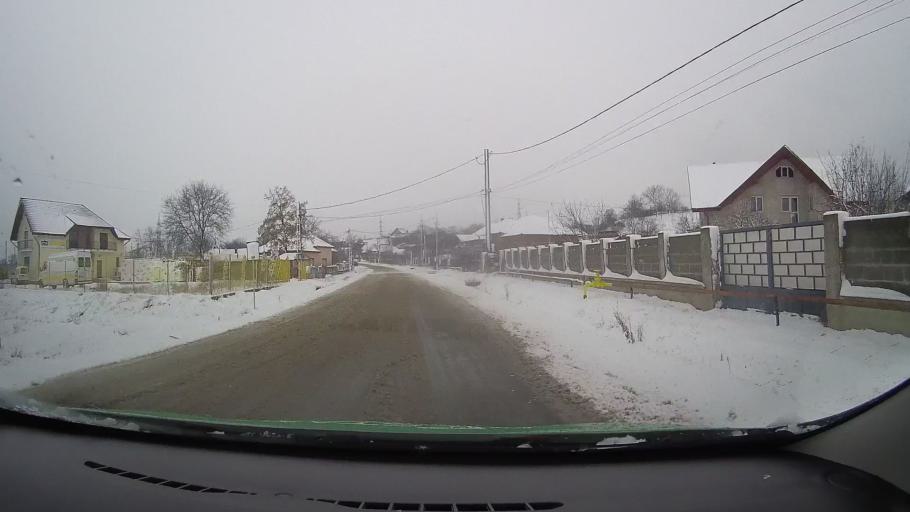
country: RO
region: Hunedoara
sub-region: Municipiul Hunedoara
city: Pestisu Mare
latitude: 45.7987
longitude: 22.9207
